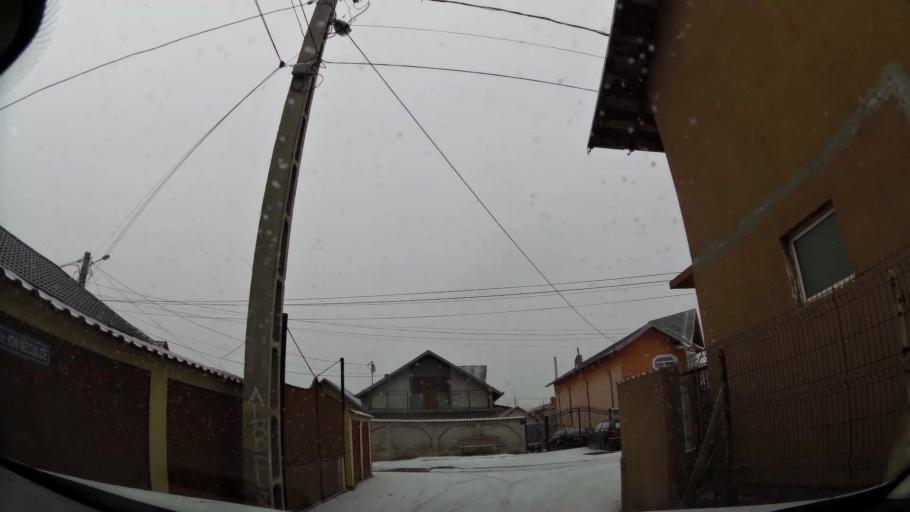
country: RO
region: Dambovita
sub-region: Comuna Ulmi
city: Ulmi
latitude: 44.9133
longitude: 25.4810
